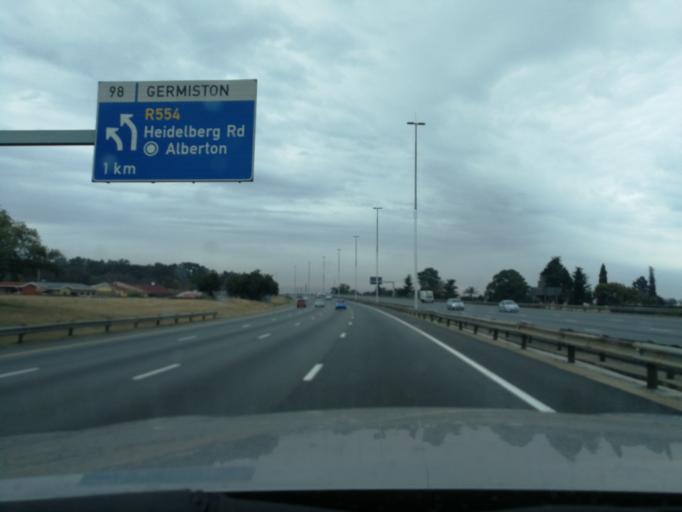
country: ZA
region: Gauteng
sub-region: Ekurhuleni Metropolitan Municipality
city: Germiston
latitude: -26.2763
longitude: 28.1491
